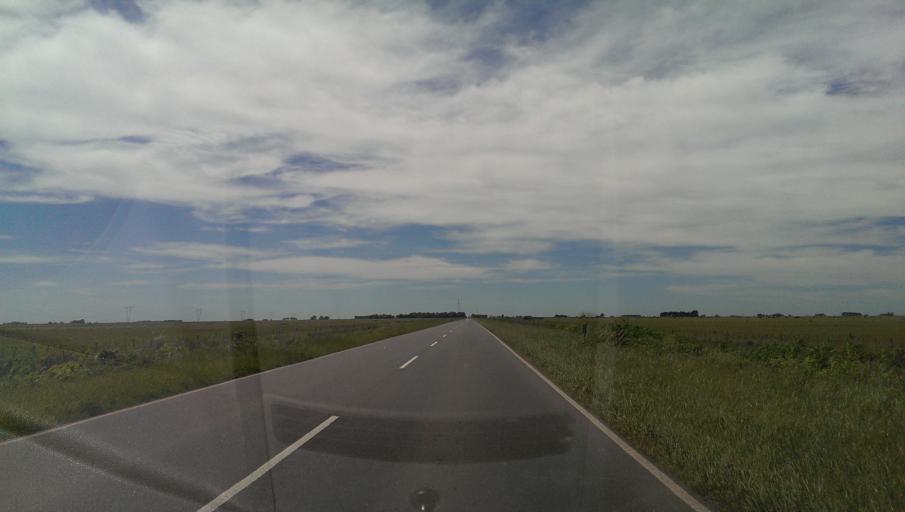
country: AR
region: Buenos Aires
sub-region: Partido de Laprida
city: Laprida
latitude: -37.2110
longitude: -60.6838
